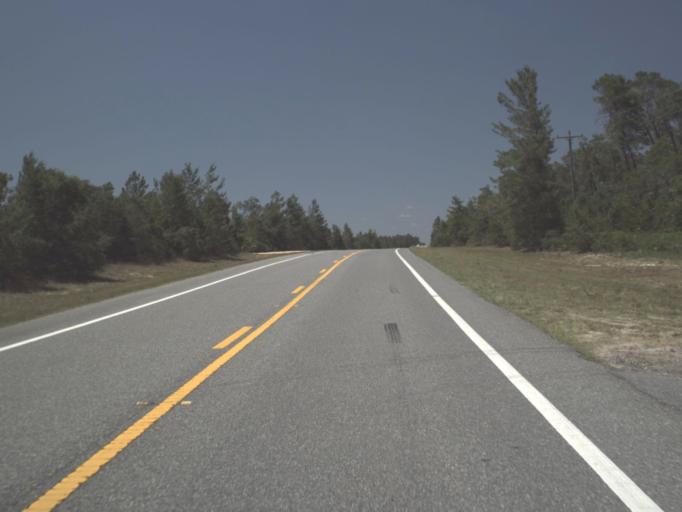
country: US
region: Florida
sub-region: Lake County
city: Astor
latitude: 29.1300
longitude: -81.6227
